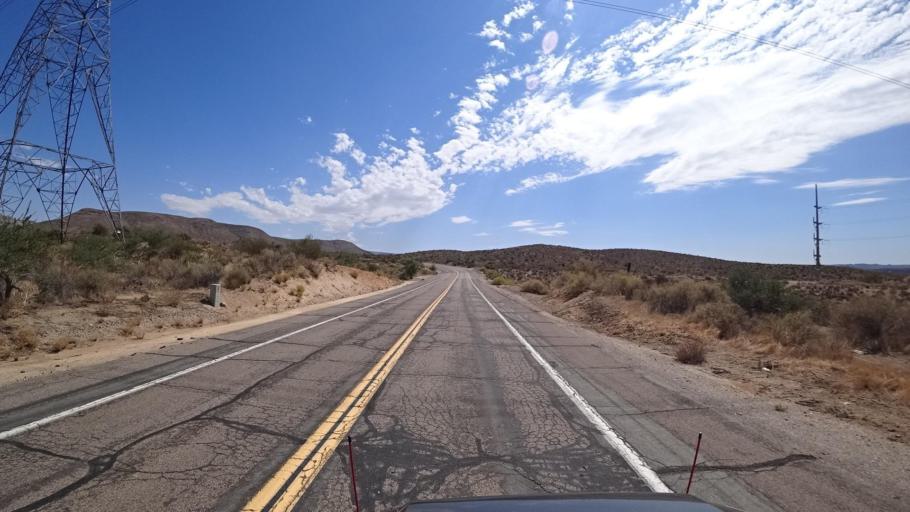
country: MX
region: Baja California
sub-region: Tecate
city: Cereso del Hongo
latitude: 32.6303
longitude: -116.1632
